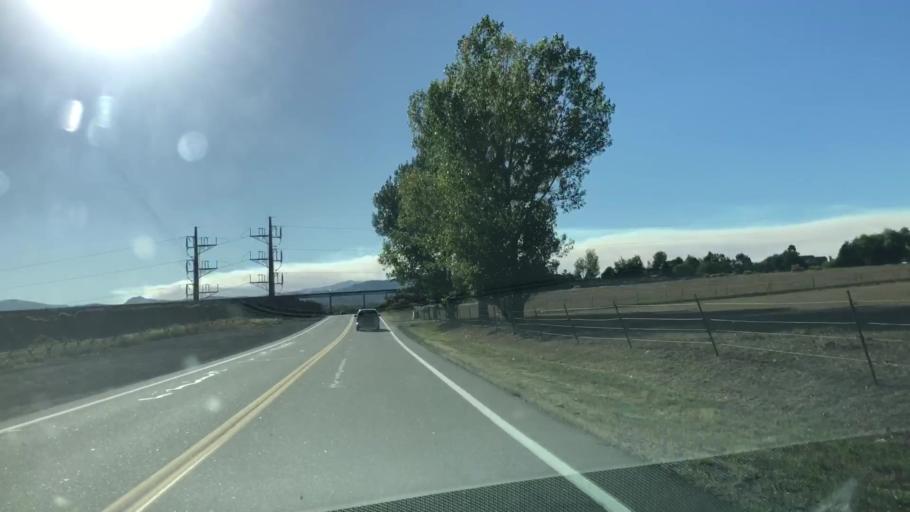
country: US
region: Colorado
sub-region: Larimer County
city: Fort Collins
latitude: 40.4947
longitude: -105.0462
